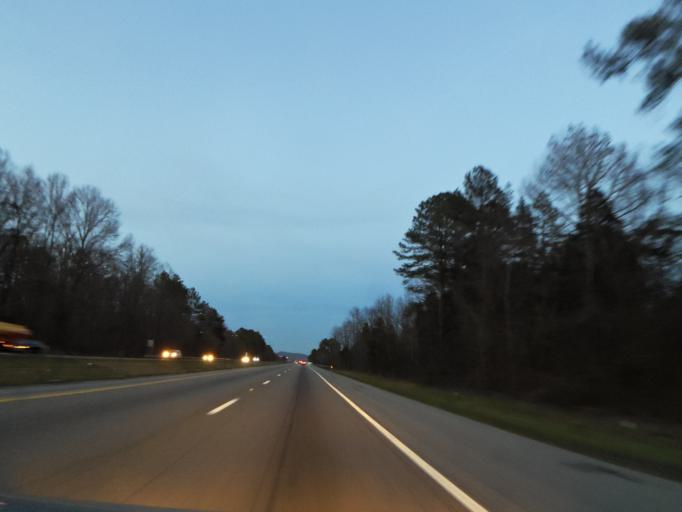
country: US
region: Tennessee
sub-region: Roane County
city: Kingston
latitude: 35.8665
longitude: -84.3862
